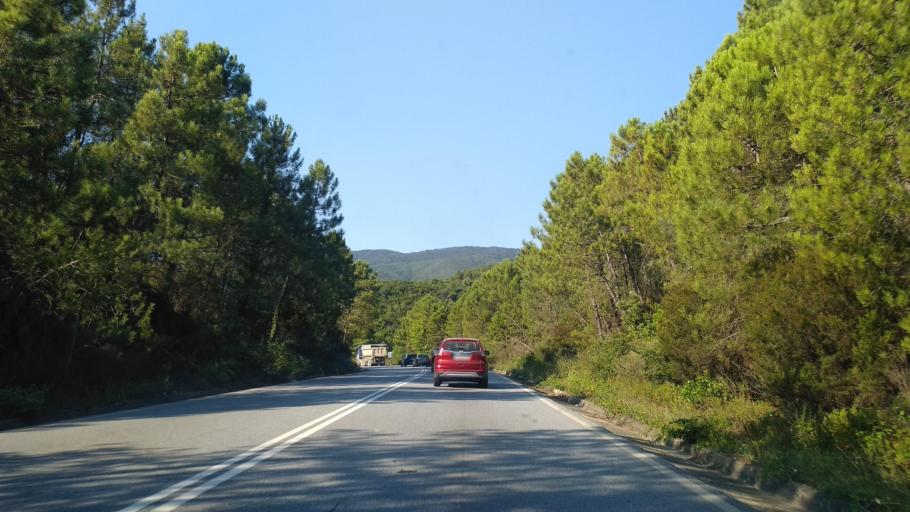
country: GR
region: Central Macedonia
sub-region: Nomos Chalkidikis
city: Stratonion
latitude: 40.5637
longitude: 23.8216
